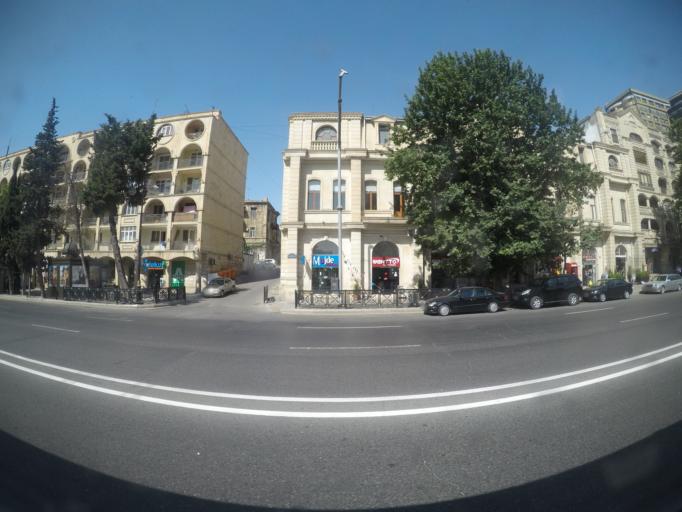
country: AZ
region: Baki
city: Badamdar
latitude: 40.3769
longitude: 49.8321
